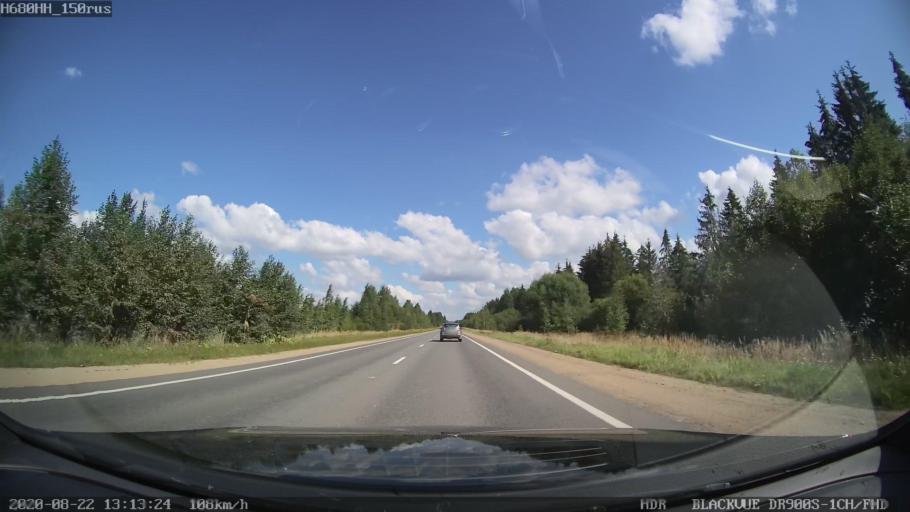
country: RU
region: Tverskaya
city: Bezhetsk
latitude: 57.7499
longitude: 36.5717
